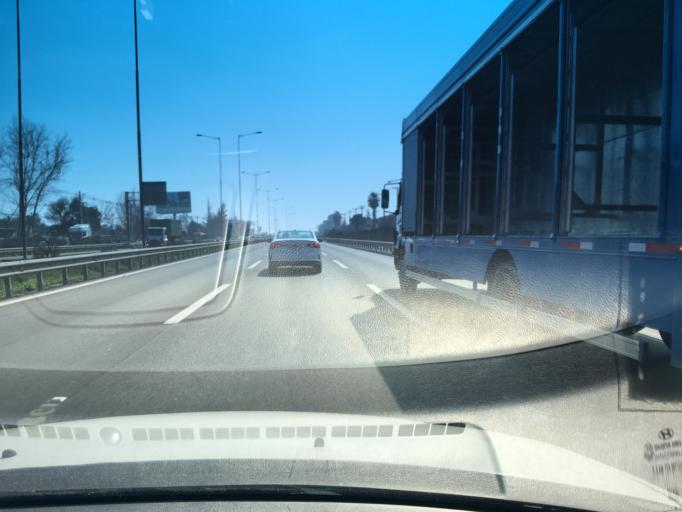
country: CL
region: Santiago Metropolitan
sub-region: Provincia de Santiago
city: Lo Prado
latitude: -33.4676
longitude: -70.7648
